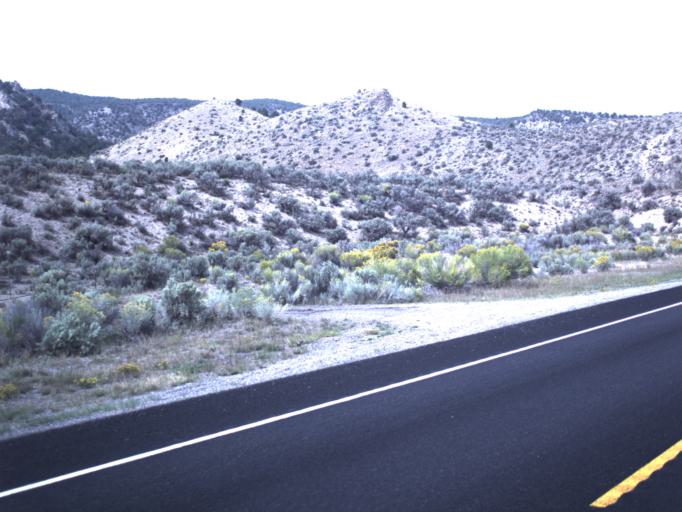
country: US
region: Utah
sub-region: Piute County
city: Junction
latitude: 38.0444
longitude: -112.3541
